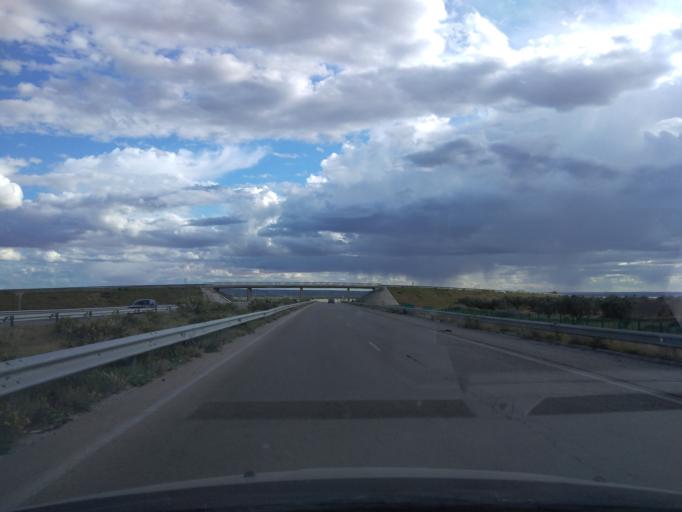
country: TN
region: Al Munastir
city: Manzil Kamil
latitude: 35.5219
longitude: 10.6264
